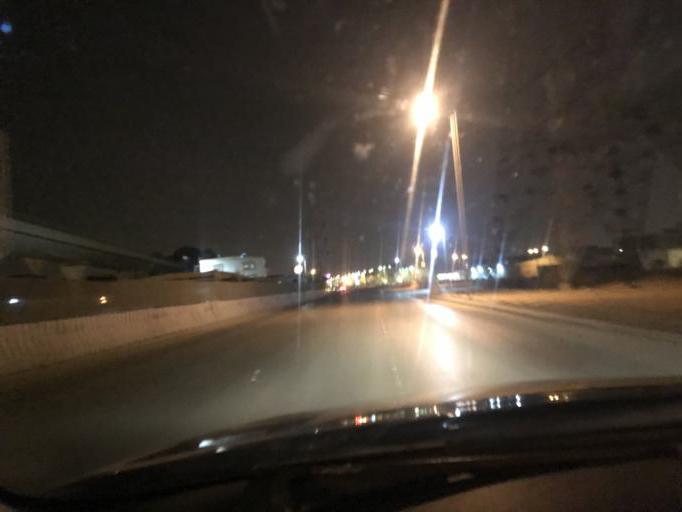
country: SA
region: Ar Riyad
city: Riyadh
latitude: 24.8001
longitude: 46.6935
